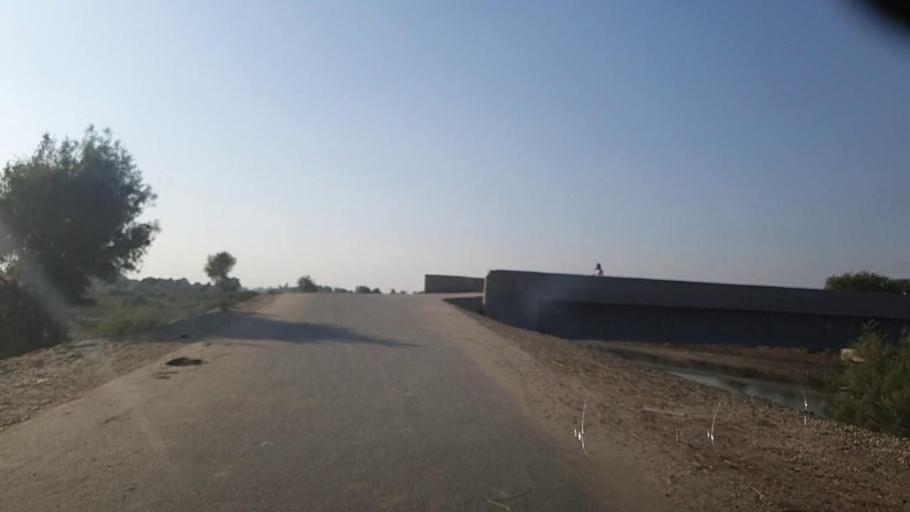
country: PK
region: Sindh
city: Tangwani
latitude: 28.3005
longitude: 68.9518
